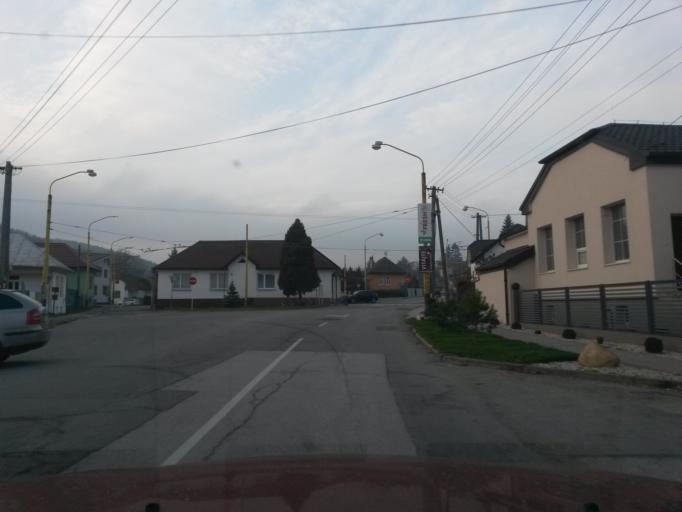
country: SK
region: Kosicky
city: Kosice
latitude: 48.7086
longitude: 21.2054
